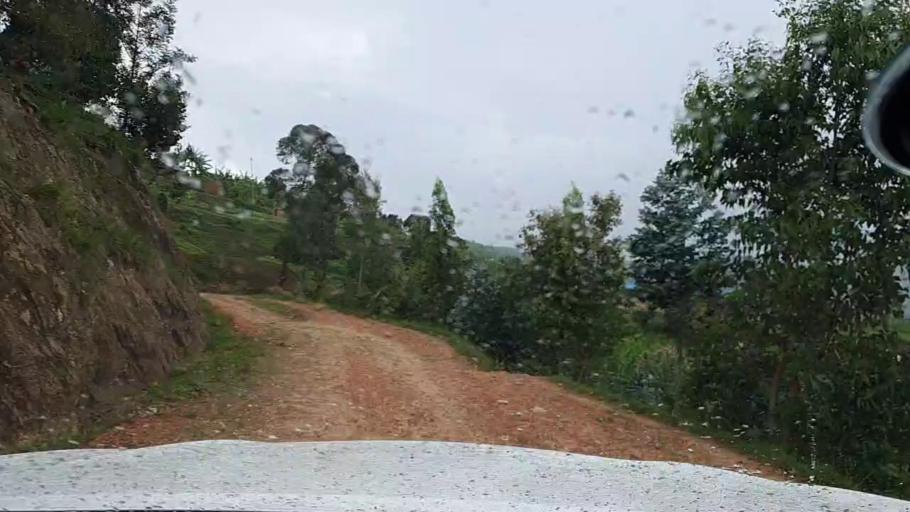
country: RW
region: Western Province
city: Kibuye
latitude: -2.0781
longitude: 29.4443
